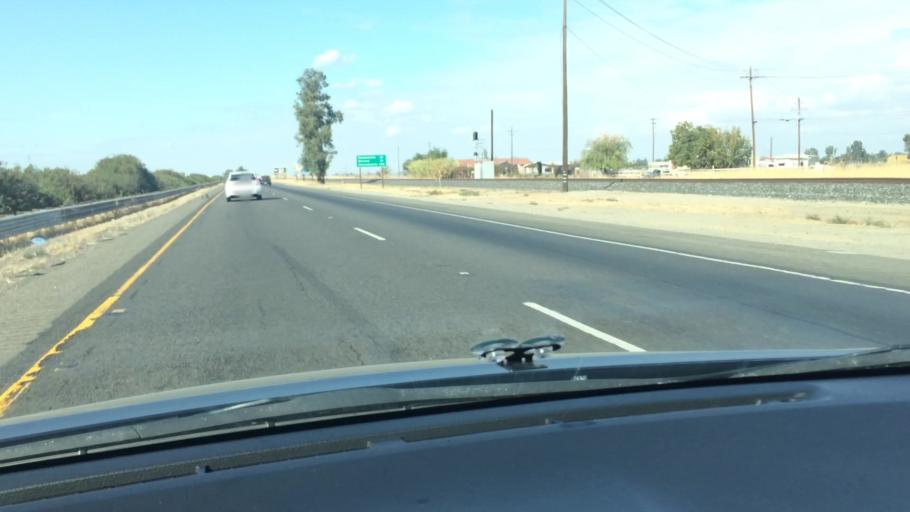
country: US
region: California
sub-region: Madera County
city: Madera
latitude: 36.9854
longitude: -120.0875
